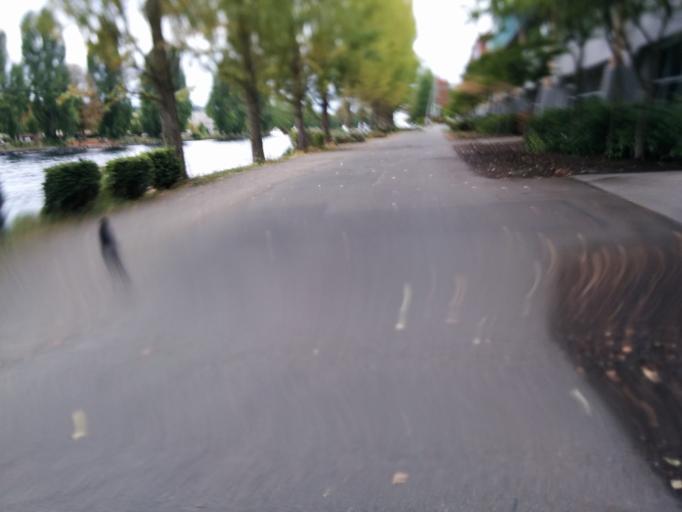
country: US
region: Washington
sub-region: King County
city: Seattle
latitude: 47.6491
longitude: -122.3518
